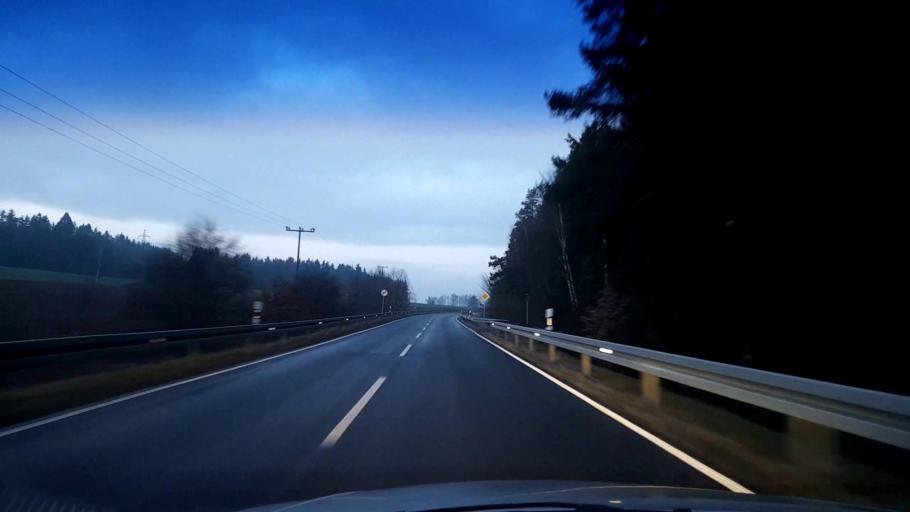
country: DE
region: Bavaria
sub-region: Upper Franconia
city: Arzberg
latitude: 50.0400
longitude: 12.2002
